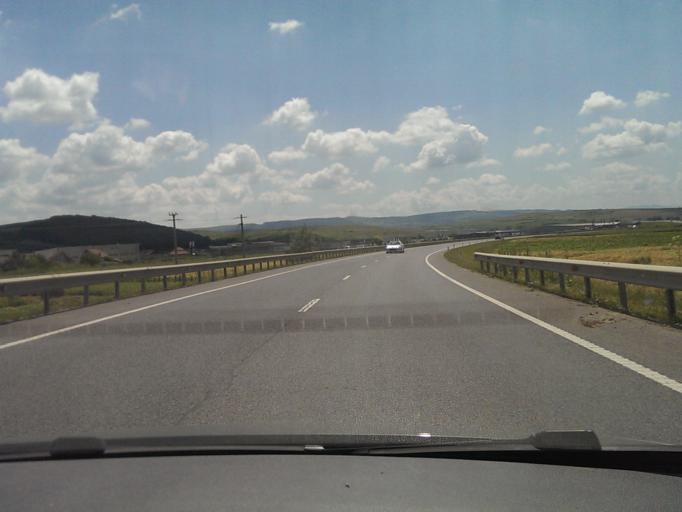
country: RO
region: Cluj
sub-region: Comuna Apahida
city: Sannicoara
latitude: 46.7882
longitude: 23.7166
